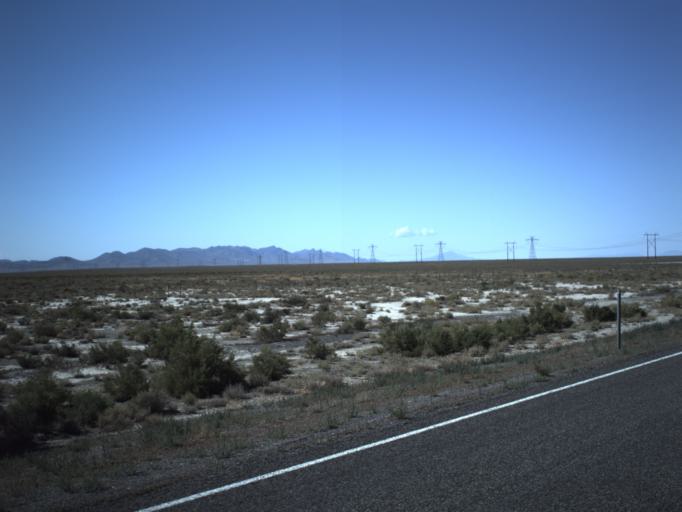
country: US
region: Utah
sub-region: Millard County
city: Delta
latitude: 39.2498
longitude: -112.8984
